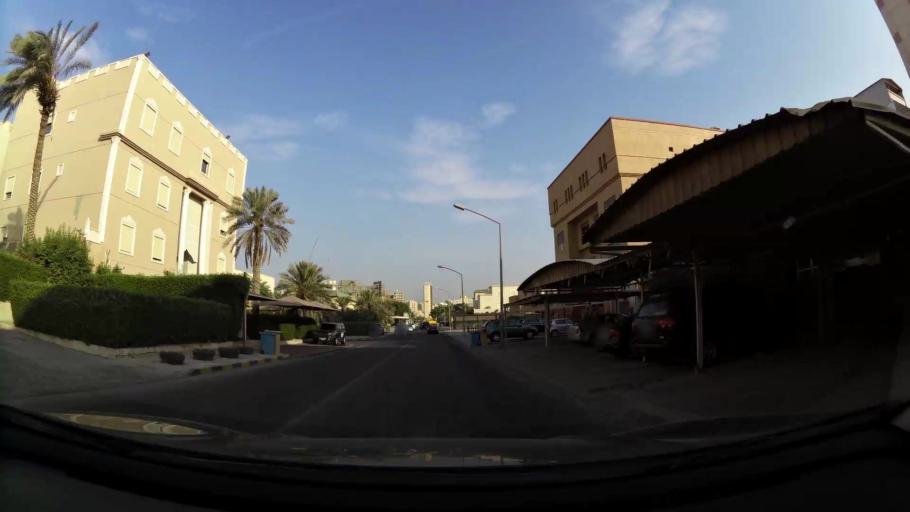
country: KW
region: Muhafazat Hawalli
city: Ar Rumaythiyah
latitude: 29.3193
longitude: 48.0729
